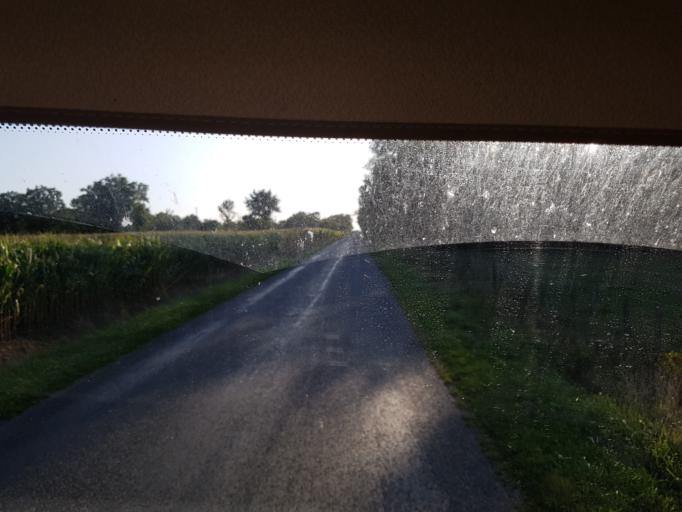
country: FR
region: Rhone-Alpes
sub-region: Departement de l'Ain
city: Villars-les-Dombes
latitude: 45.9645
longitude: 5.0580
